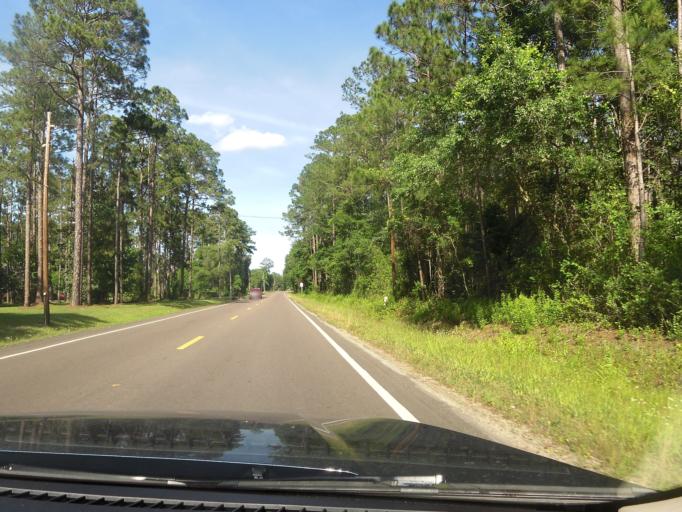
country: US
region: Florida
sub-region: Nassau County
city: Callahan
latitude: 30.5568
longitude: -81.8707
